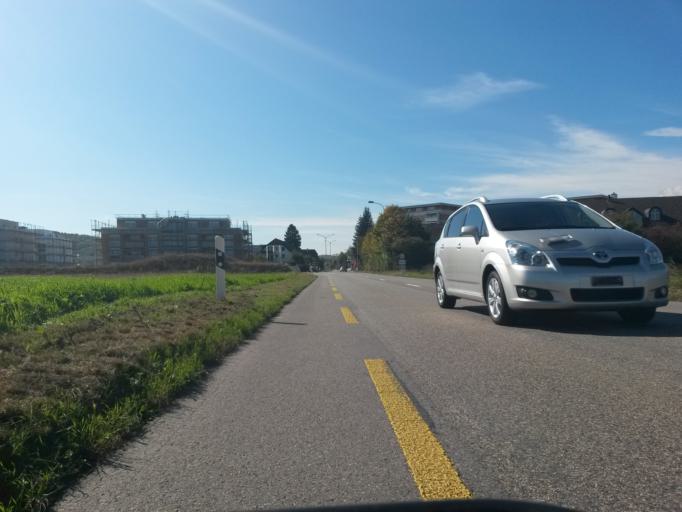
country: CH
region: Solothurn
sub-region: Bezirk Wasseramt
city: Zuchwil
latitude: 47.2112
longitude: 7.5658
